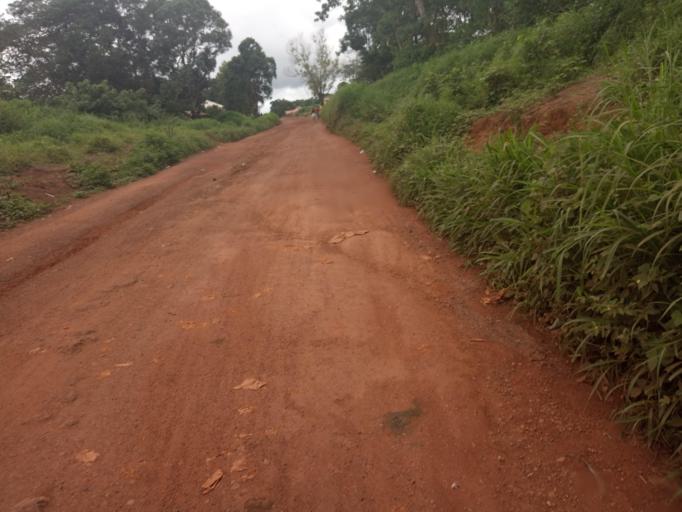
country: SL
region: Northern Province
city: Kamakwie
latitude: 9.4980
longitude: -12.2470
